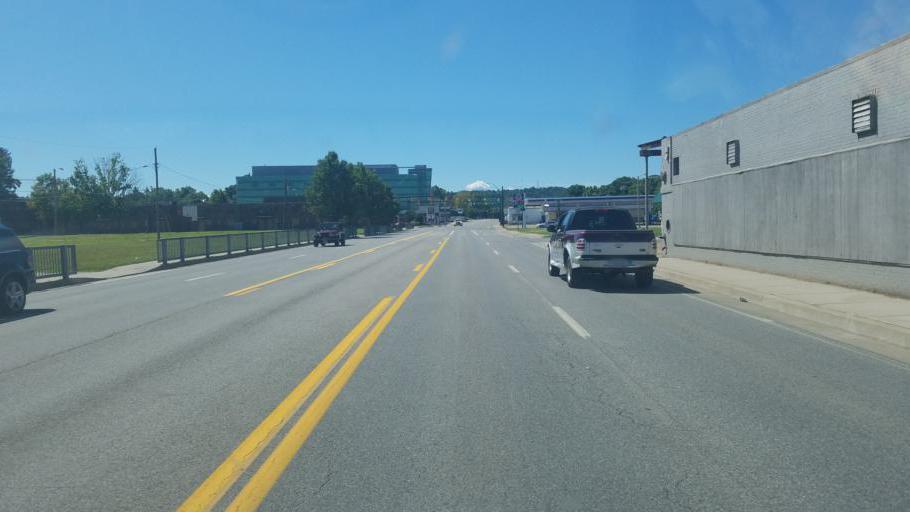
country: US
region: West Virginia
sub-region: Cabell County
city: Huntington
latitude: 38.4137
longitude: -82.4293
